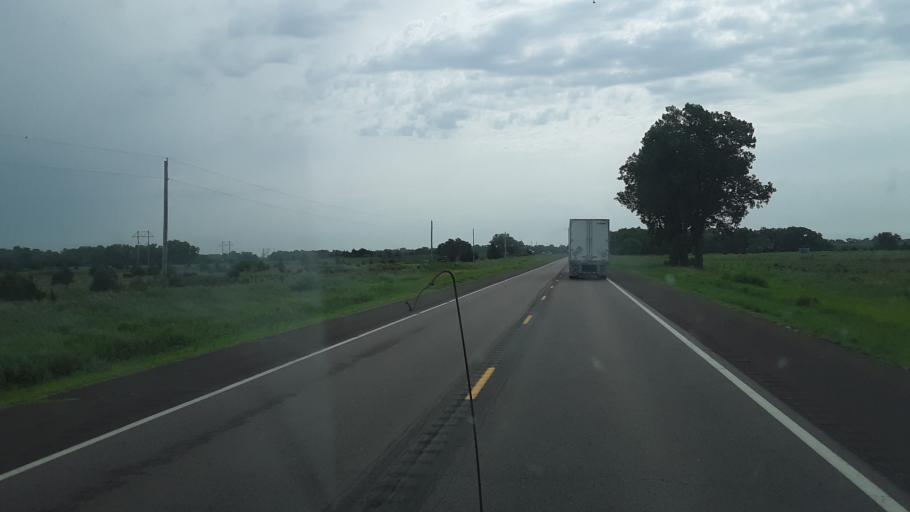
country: US
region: Kansas
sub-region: Stafford County
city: Saint John
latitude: 37.9558
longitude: -98.7360
